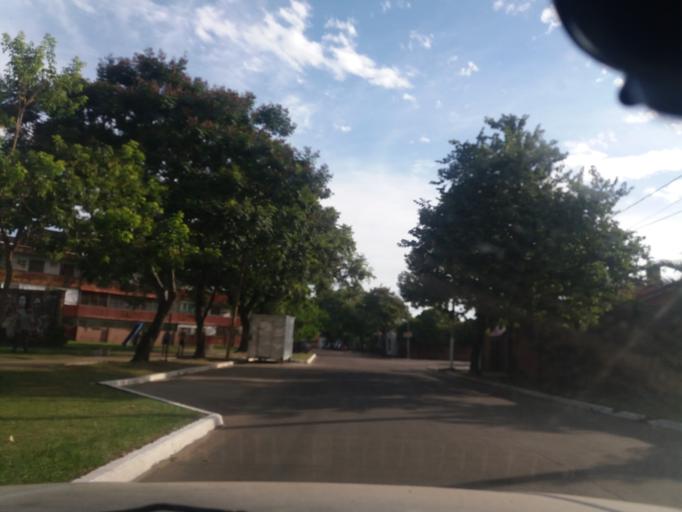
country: AR
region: Corrientes
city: Corrientes
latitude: -27.4834
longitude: -58.8310
